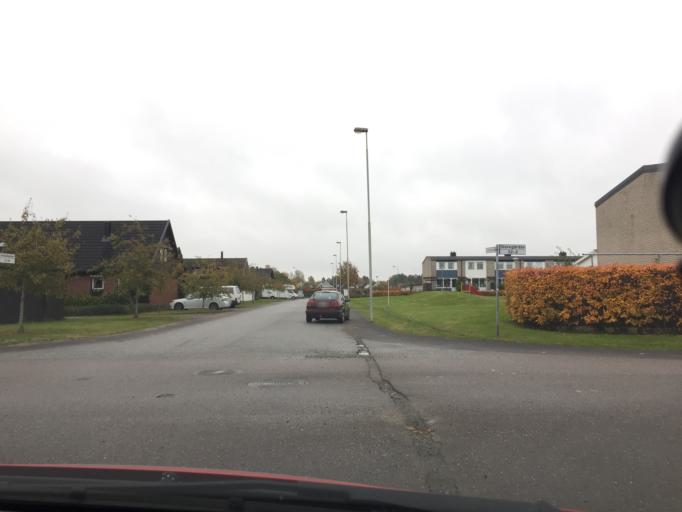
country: SE
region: Vaestra Goetaland
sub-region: Trollhattan
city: Trollhattan
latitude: 58.2844
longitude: 12.3224
